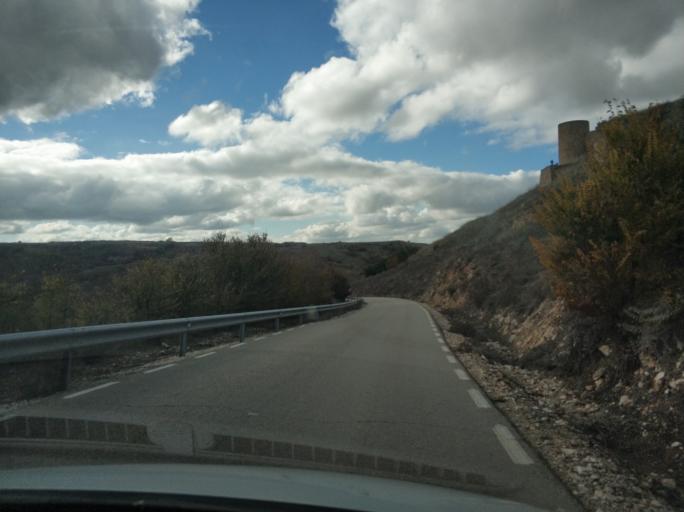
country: ES
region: Castille and Leon
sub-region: Provincia de Soria
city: Medinaceli
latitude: 41.1695
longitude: -2.4349
